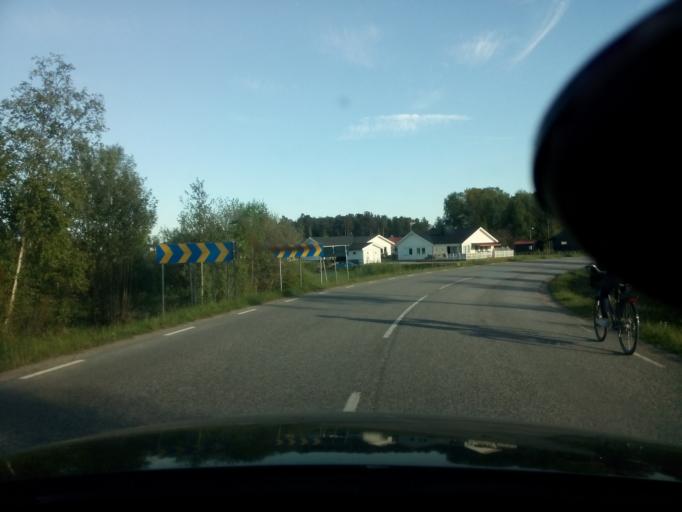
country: SE
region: Soedermanland
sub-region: Nykopings Kommun
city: Nykoping
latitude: 58.7804
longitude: 17.0066
